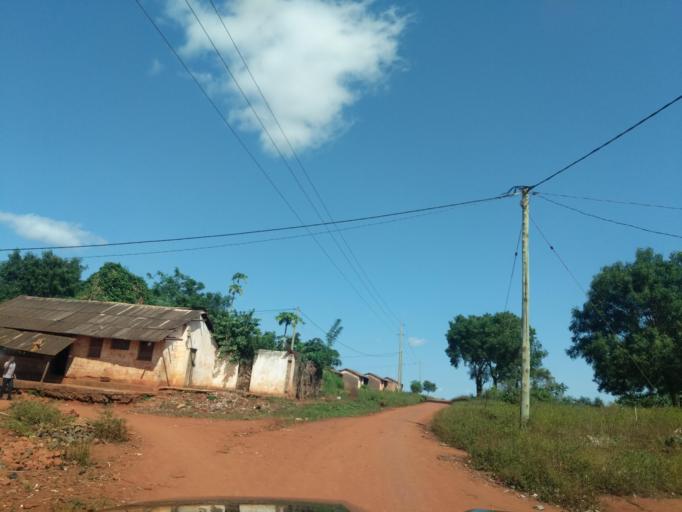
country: TZ
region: Tanga
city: Muheza
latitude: -5.3867
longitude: 38.5764
